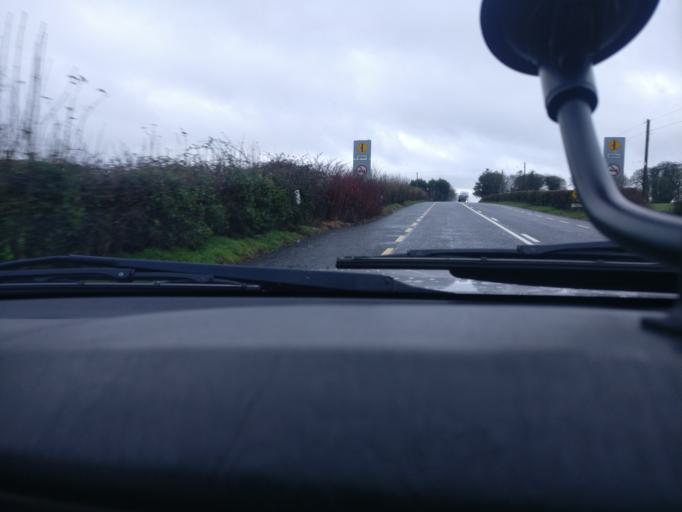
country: IE
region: Leinster
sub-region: An Mhi
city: Enfield
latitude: 53.4228
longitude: -6.8642
